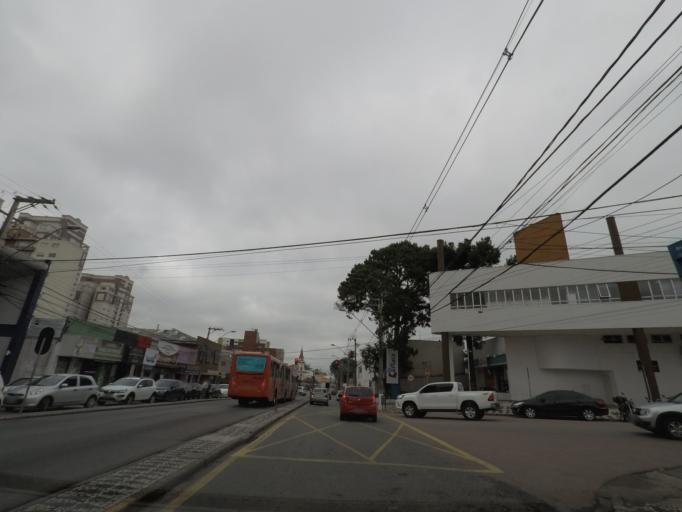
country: BR
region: Parana
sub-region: Curitiba
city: Curitiba
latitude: -25.4706
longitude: -49.2945
